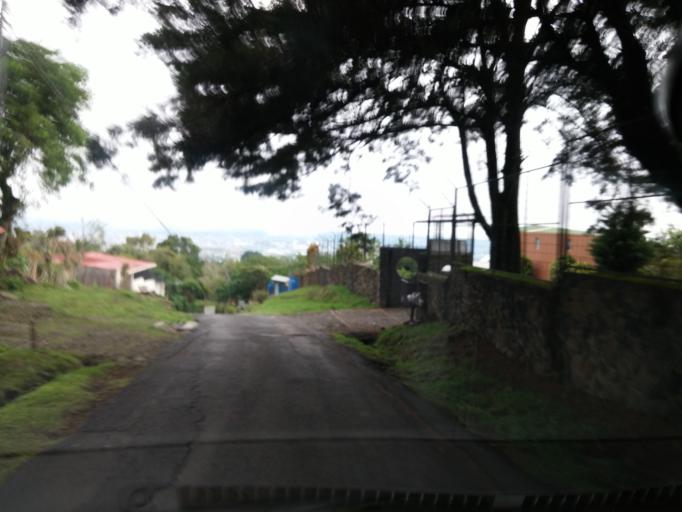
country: CR
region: Heredia
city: San Josecito
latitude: 10.0332
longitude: -84.0967
